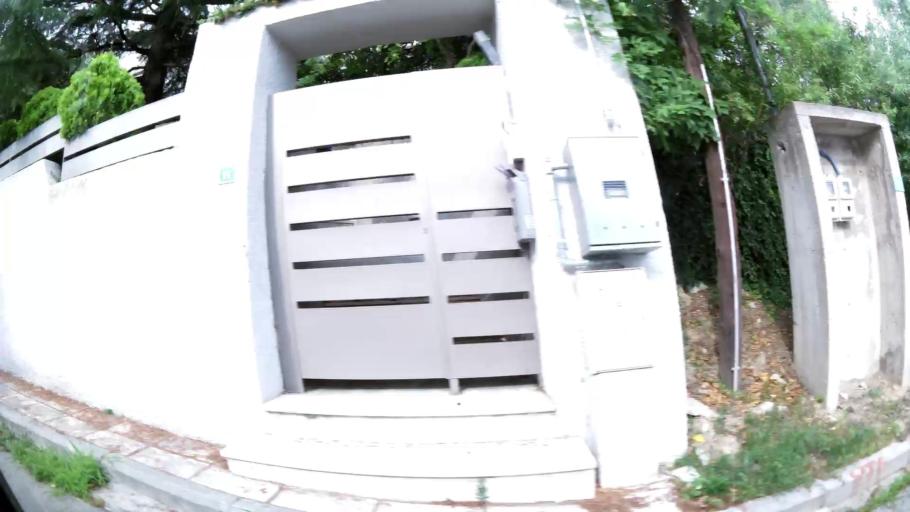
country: GR
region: Central Macedonia
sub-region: Nomos Thessalonikis
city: Oraiokastro
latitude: 40.7331
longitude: 22.9226
